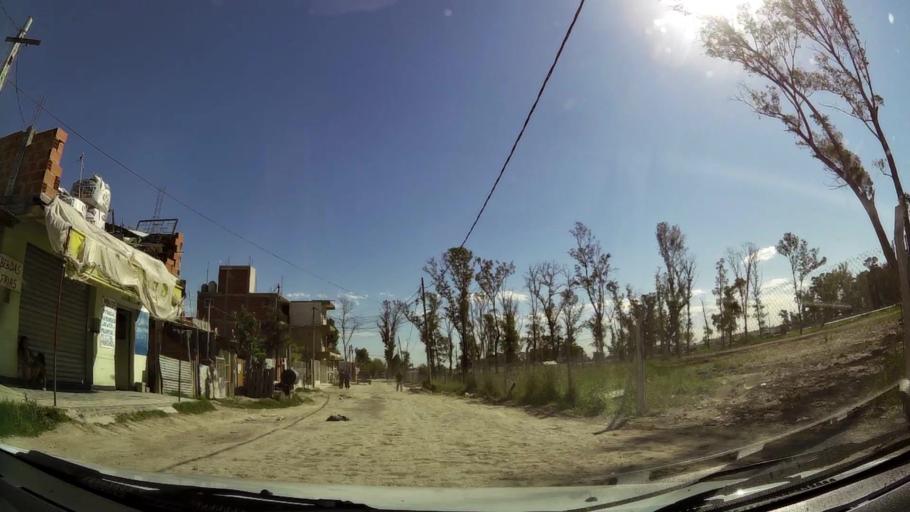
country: AR
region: Buenos Aires
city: Hurlingham
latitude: -34.5306
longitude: -58.5926
